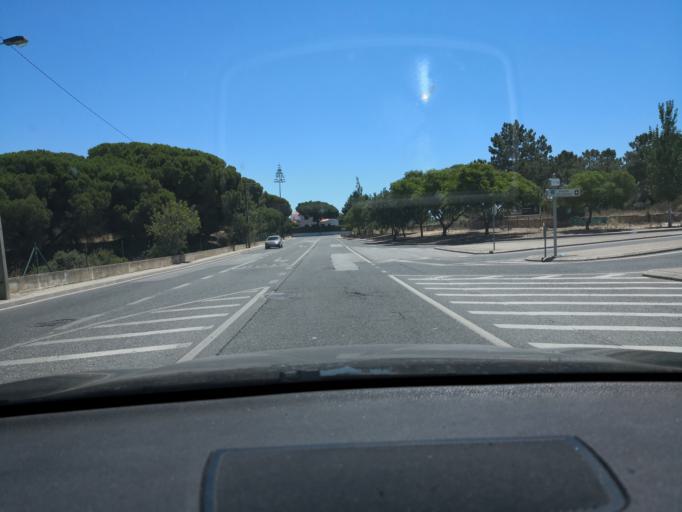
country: PT
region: Faro
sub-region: Albufeira
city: Ferreiras
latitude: 37.1083
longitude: -8.2020
